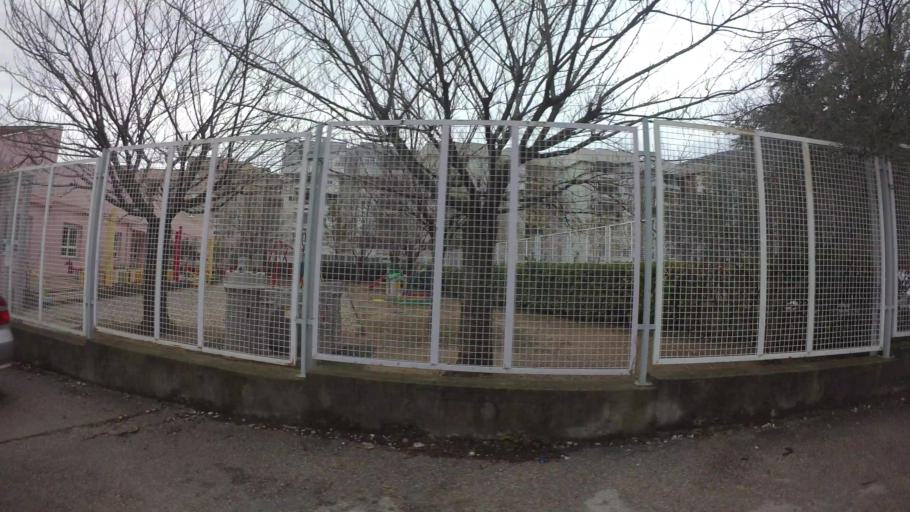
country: BA
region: Federation of Bosnia and Herzegovina
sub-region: Hercegovacko-Bosanski Kanton
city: Mostar
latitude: 43.3387
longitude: 17.8001
